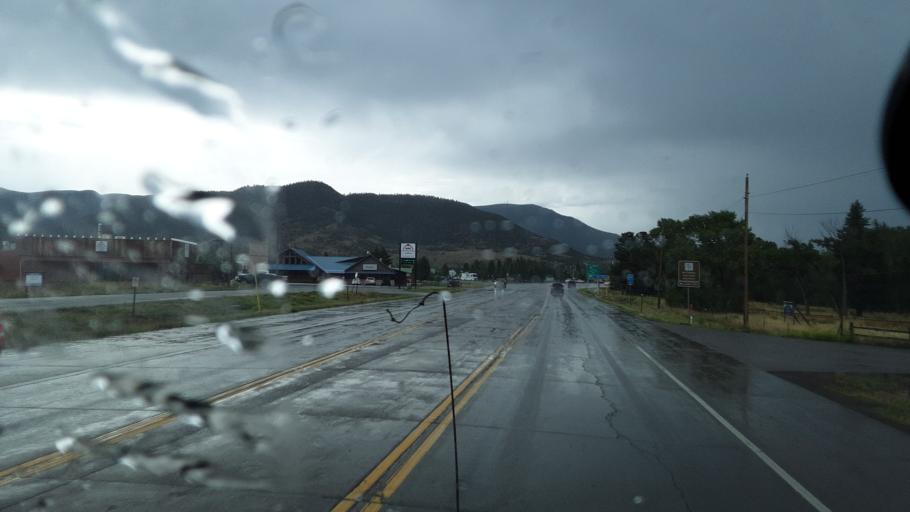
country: US
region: Colorado
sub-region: Rio Grande County
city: Del Norte
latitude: 37.6662
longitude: -106.6441
